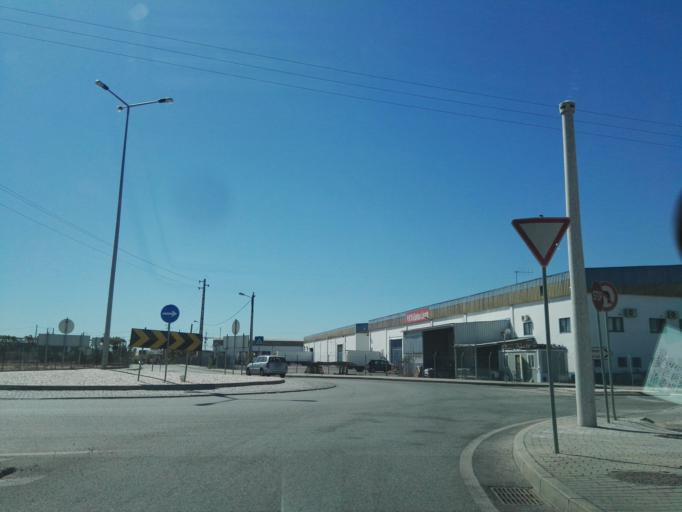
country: PT
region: Santarem
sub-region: Benavente
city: Samora Correia
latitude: 38.9181
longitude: -8.8525
